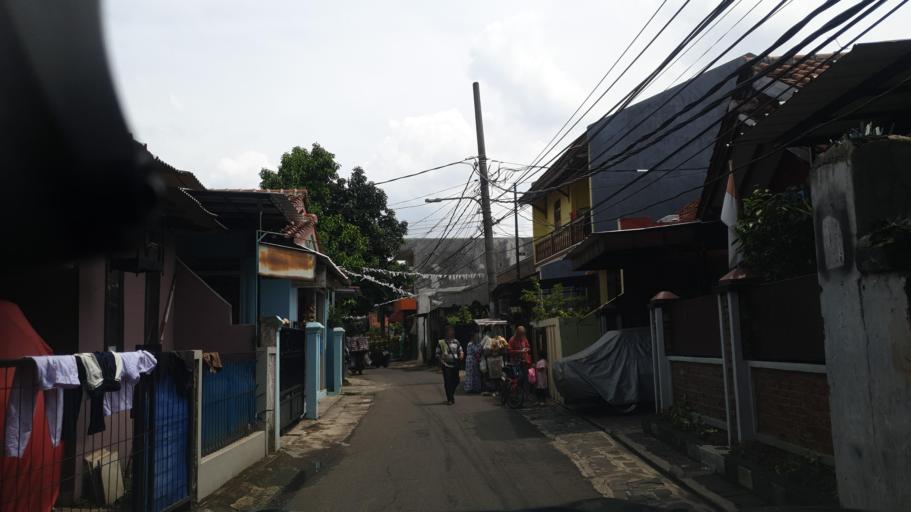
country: ID
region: West Java
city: Pamulang
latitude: -6.3388
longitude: 106.7698
